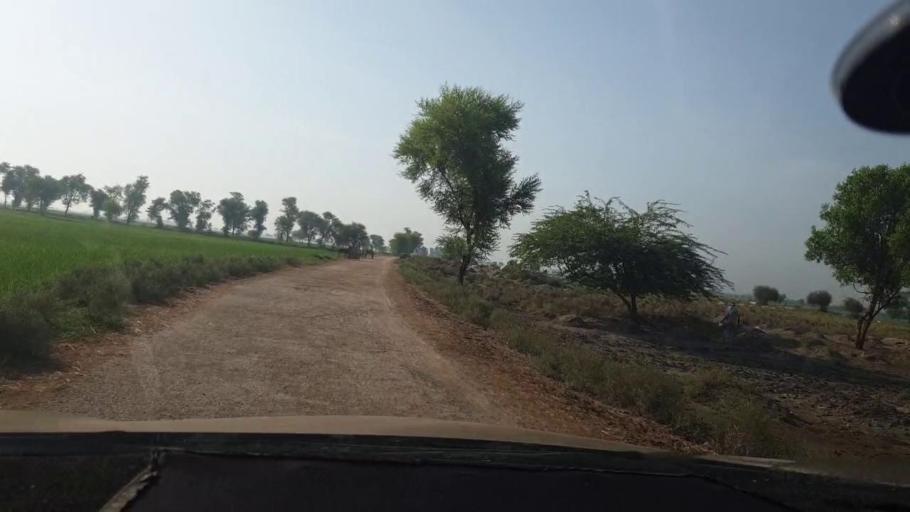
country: PK
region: Sindh
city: Kambar
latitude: 27.6439
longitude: 68.0429
